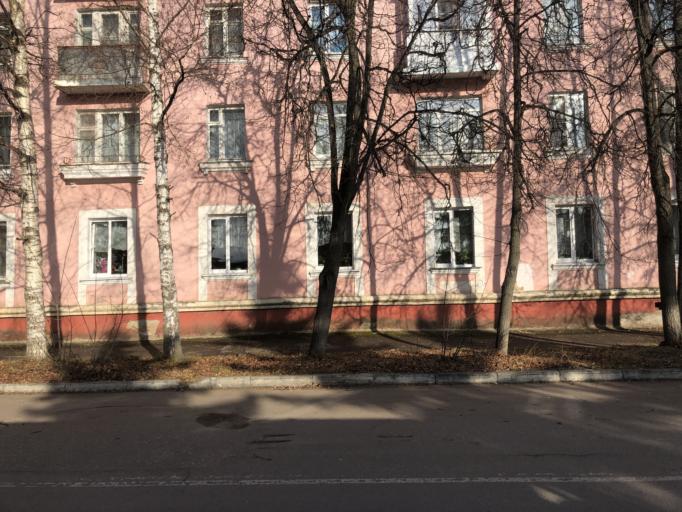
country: RU
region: Tverskaya
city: Rzhev
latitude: 56.2628
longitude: 34.3310
